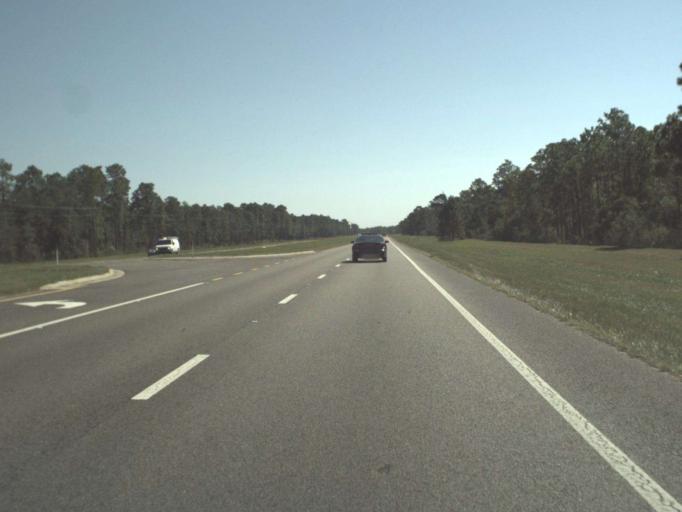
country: US
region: Florida
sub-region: Walton County
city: Seaside
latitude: 30.3632
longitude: -86.1715
